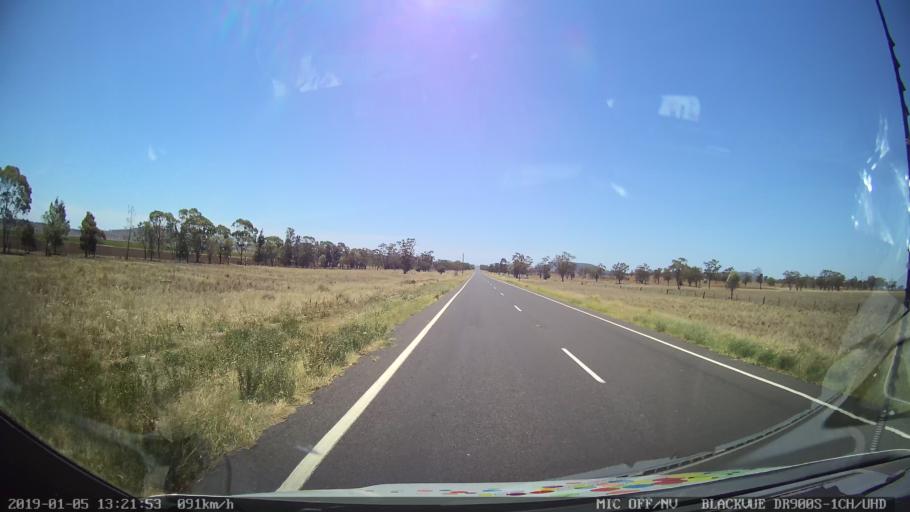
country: AU
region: New South Wales
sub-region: Gunnedah
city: Gunnedah
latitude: -31.0907
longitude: 149.9546
